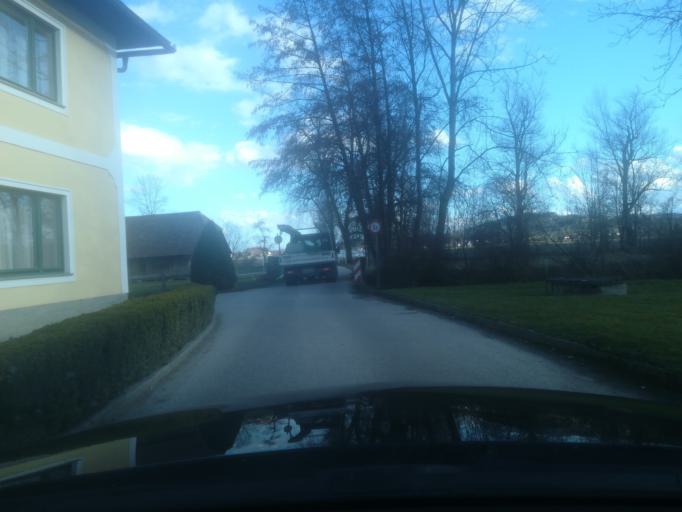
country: AT
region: Upper Austria
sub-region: Wels-Land
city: Buchkirchen
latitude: 48.2835
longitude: 14.0167
